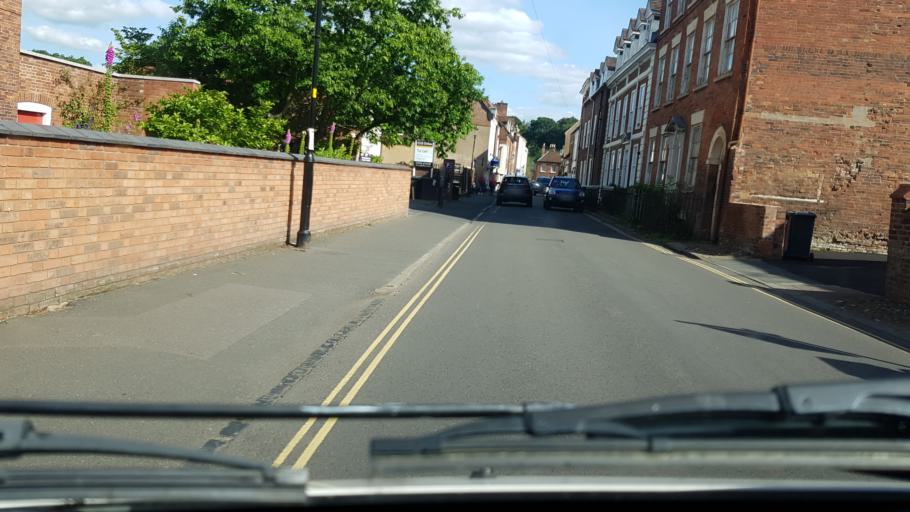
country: GB
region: England
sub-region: Worcestershire
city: Bewdley
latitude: 52.3747
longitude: -2.3151
